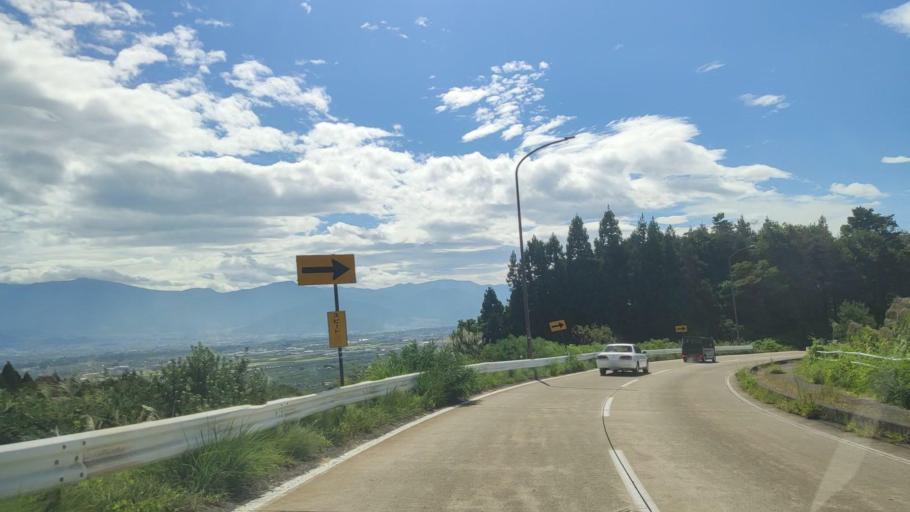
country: JP
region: Nagano
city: Suzaka
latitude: 36.7103
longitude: 138.2509
